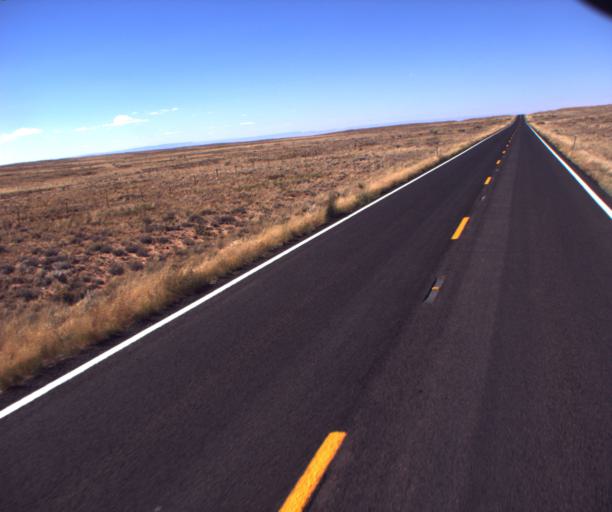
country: US
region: Arizona
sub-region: Coconino County
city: Tuba City
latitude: 35.9666
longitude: -110.9533
